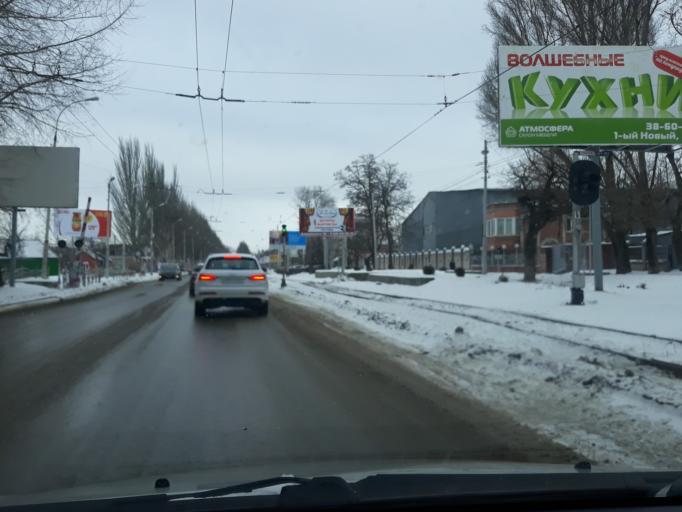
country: RU
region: Rostov
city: Taganrog
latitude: 47.2405
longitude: 38.9173
